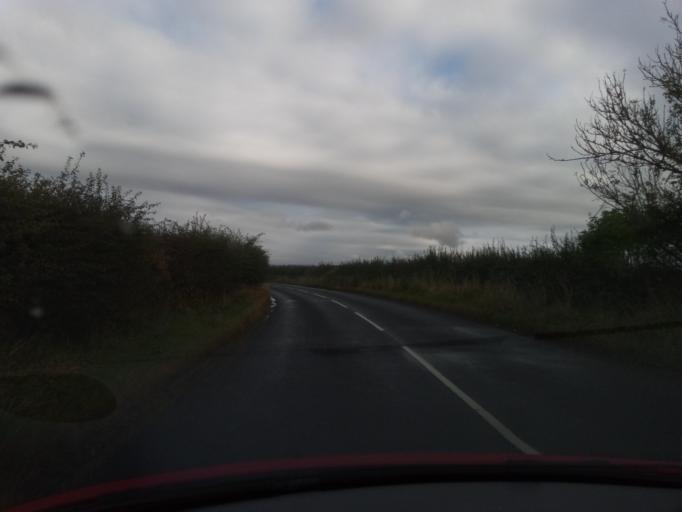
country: GB
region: Scotland
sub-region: The Scottish Borders
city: Newtown St Boswells
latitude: 55.5643
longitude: -2.6771
